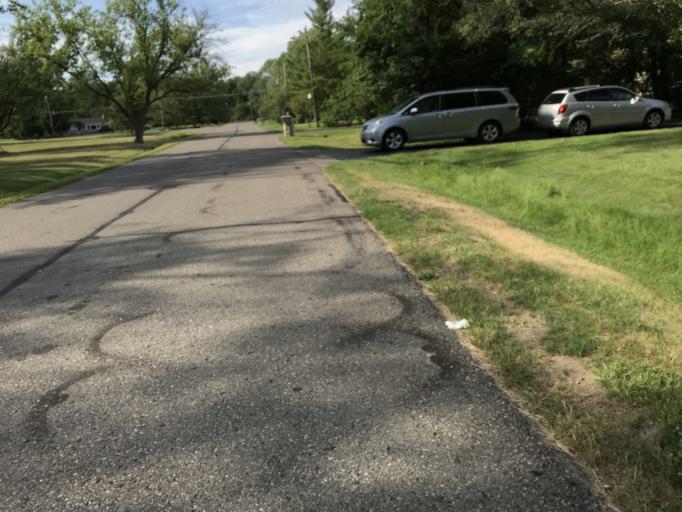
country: US
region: Michigan
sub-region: Oakland County
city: Franklin
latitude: 42.4741
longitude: -83.3244
